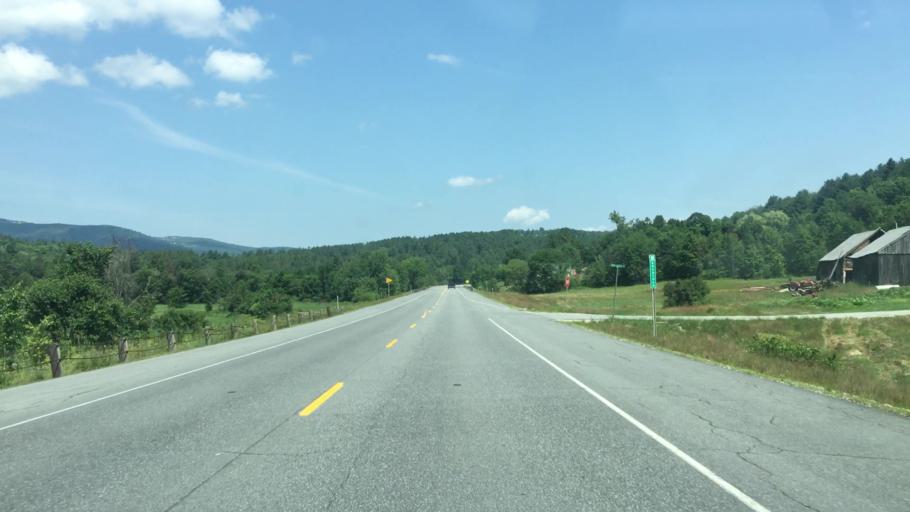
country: US
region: New Hampshire
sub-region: Sullivan County
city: Grantham
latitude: 43.4702
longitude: -72.1484
